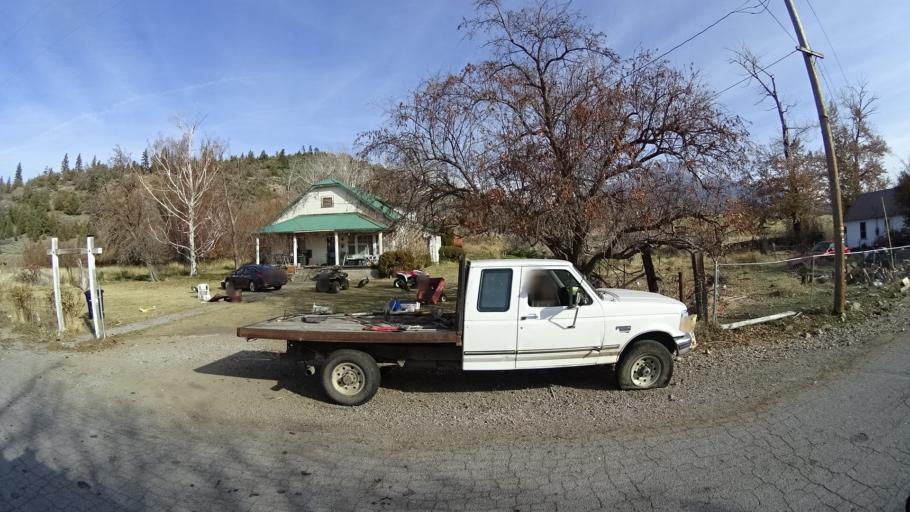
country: US
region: California
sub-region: Siskiyou County
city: Weed
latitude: 41.4647
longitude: -122.3871
